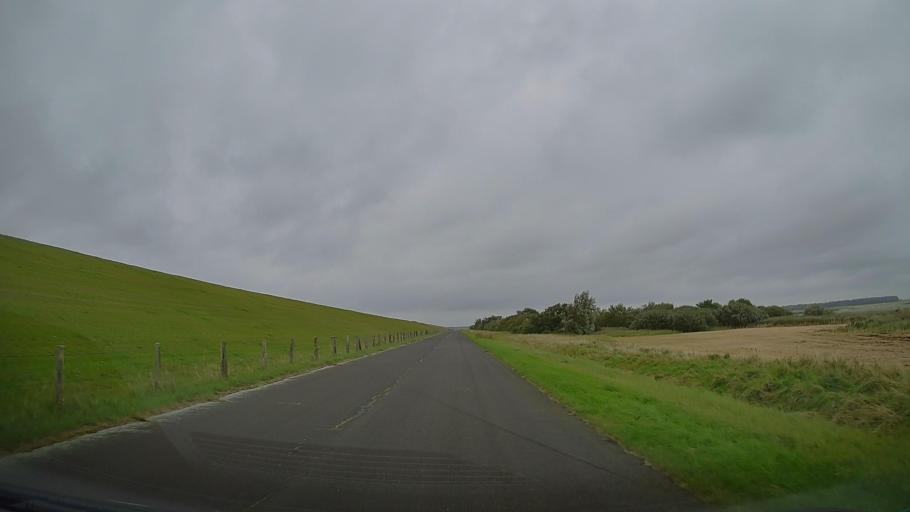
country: DE
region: Schleswig-Holstein
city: Busenwurth
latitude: 54.0471
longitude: 8.9834
